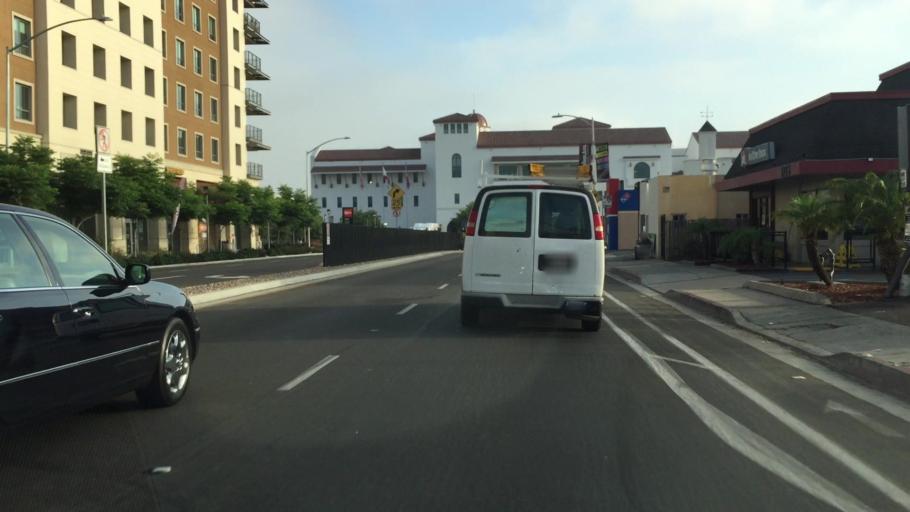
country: US
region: California
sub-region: San Diego County
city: La Mesa
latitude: 32.7718
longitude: -117.0699
